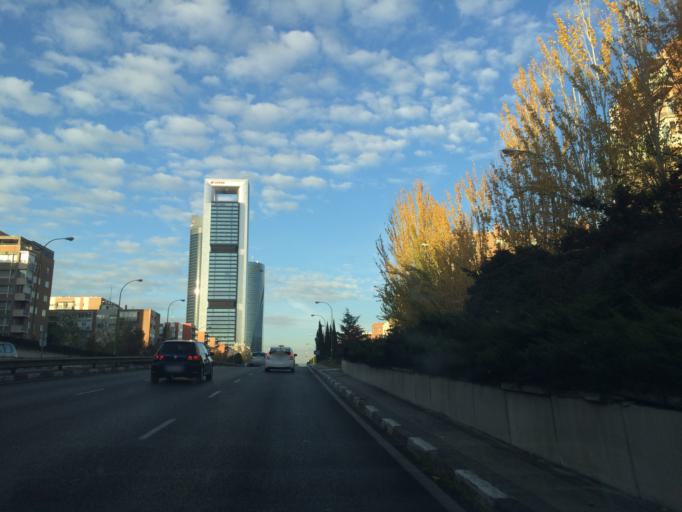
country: ES
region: Madrid
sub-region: Provincia de Madrid
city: Chamartin
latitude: 40.4691
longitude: -3.6884
